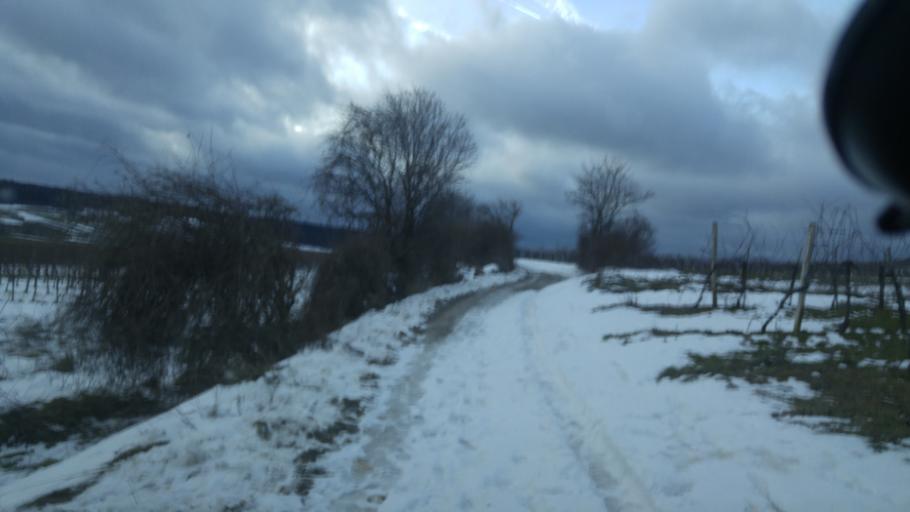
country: AT
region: Lower Austria
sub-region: Politischer Bezirk Baden
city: Hirtenberg
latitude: 47.9645
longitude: 16.1752
